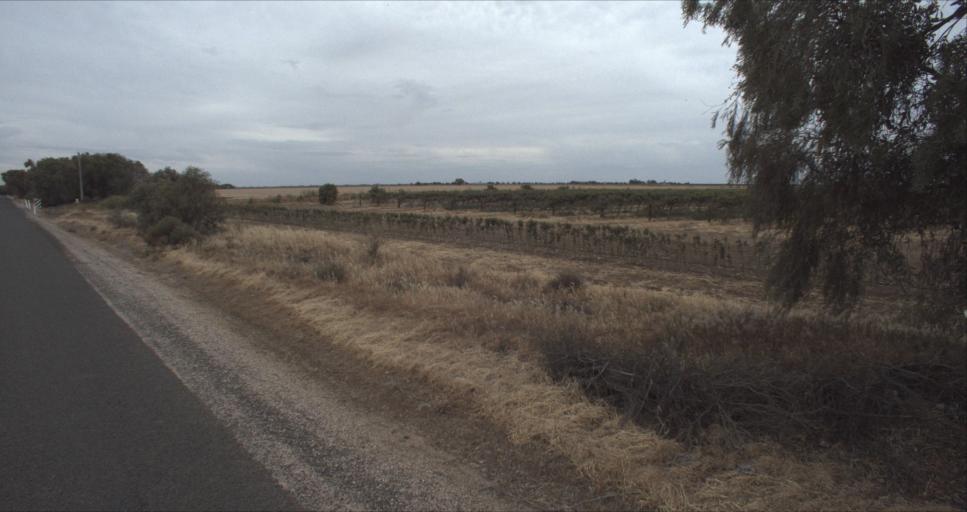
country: AU
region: New South Wales
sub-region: Leeton
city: Leeton
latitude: -34.4710
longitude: 146.3958
